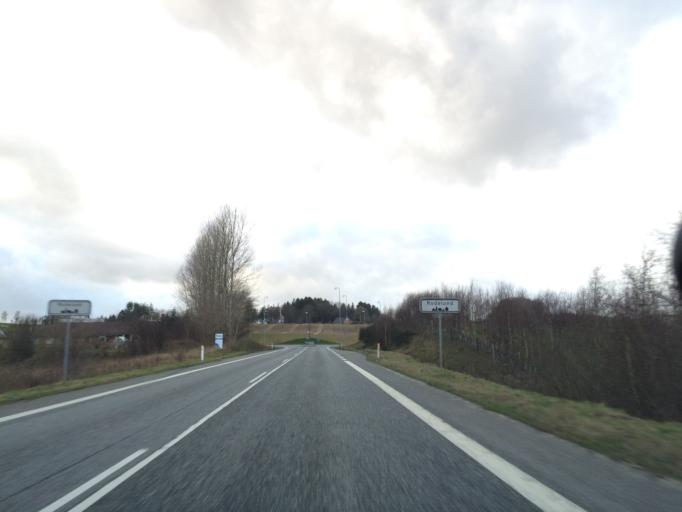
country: DK
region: Central Jutland
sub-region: Silkeborg Kommune
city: Virklund
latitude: 56.1053
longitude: 9.5776
